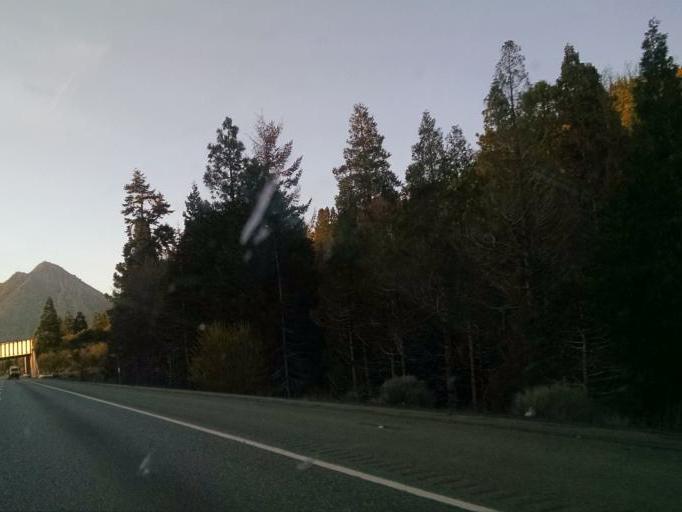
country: US
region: California
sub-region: Siskiyou County
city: Mount Shasta
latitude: 41.3287
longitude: -122.3302
